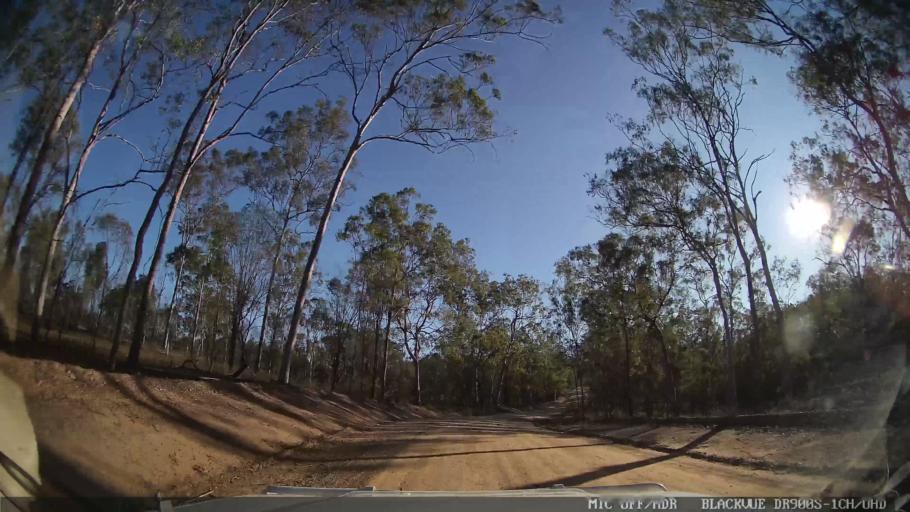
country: AU
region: Queensland
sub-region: Bundaberg
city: Sharon
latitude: -24.7361
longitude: 151.5212
